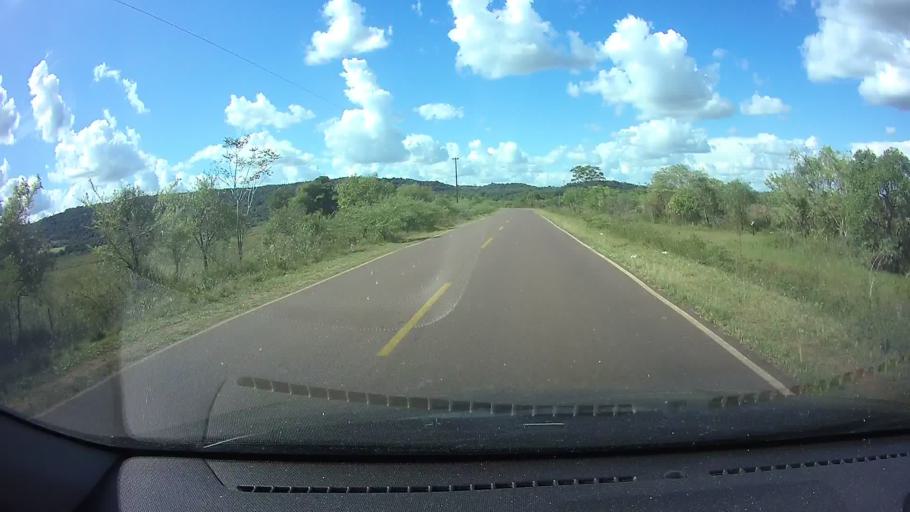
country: PY
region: Paraguari
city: Sapucai
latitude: -25.6813
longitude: -56.8629
